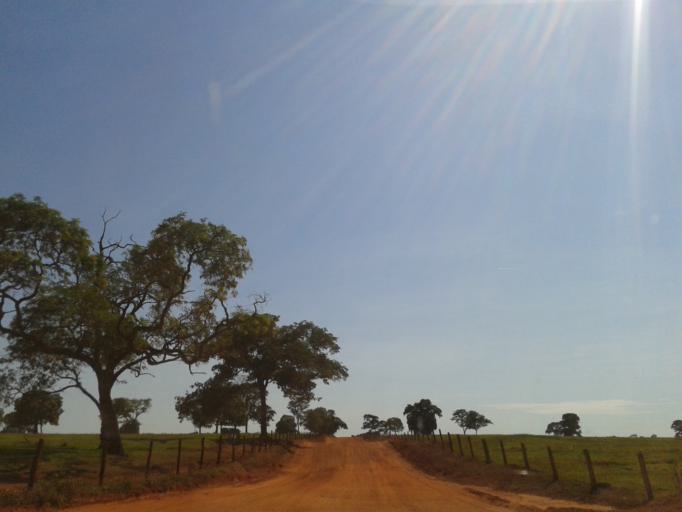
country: BR
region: Minas Gerais
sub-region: Santa Vitoria
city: Santa Vitoria
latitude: -19.1000
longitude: -50.5032
